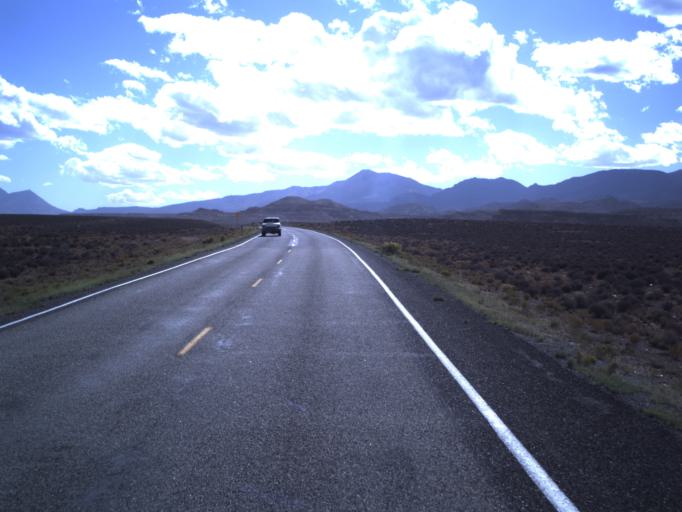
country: US
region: Utah
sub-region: Wayne County
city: Loa
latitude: 38.1230
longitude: -110.6193
